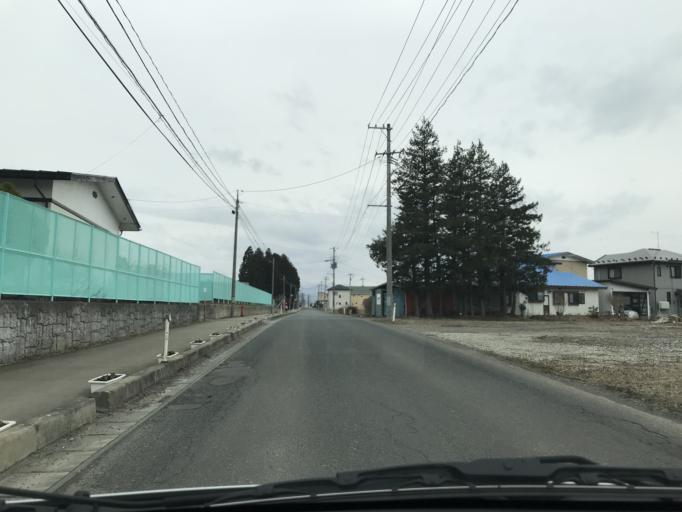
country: JP
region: Iwate
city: Hanamaki
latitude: 39.3379
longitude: 141.0898
